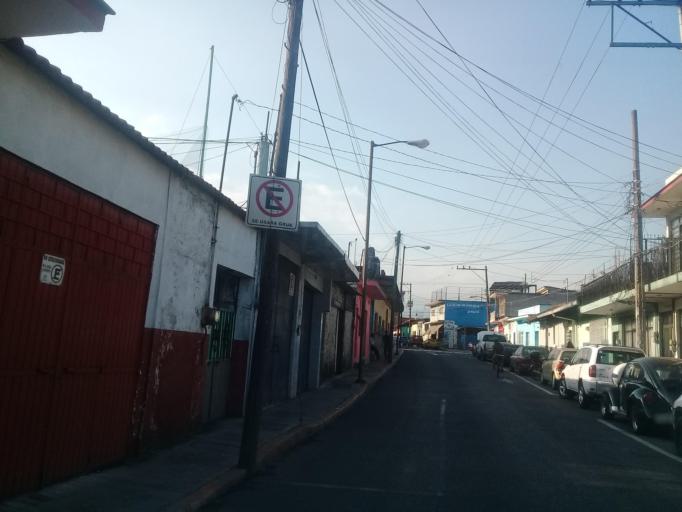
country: MX
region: Veracruz
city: Orizaba
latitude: 18.8523
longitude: -97.1086
